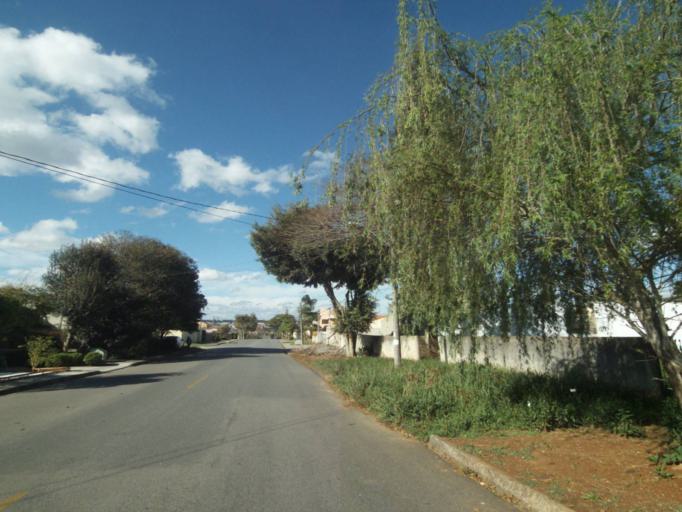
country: BR
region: Parana
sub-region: Curitiba
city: Curitiba
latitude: -25.3903
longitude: -49.2546
